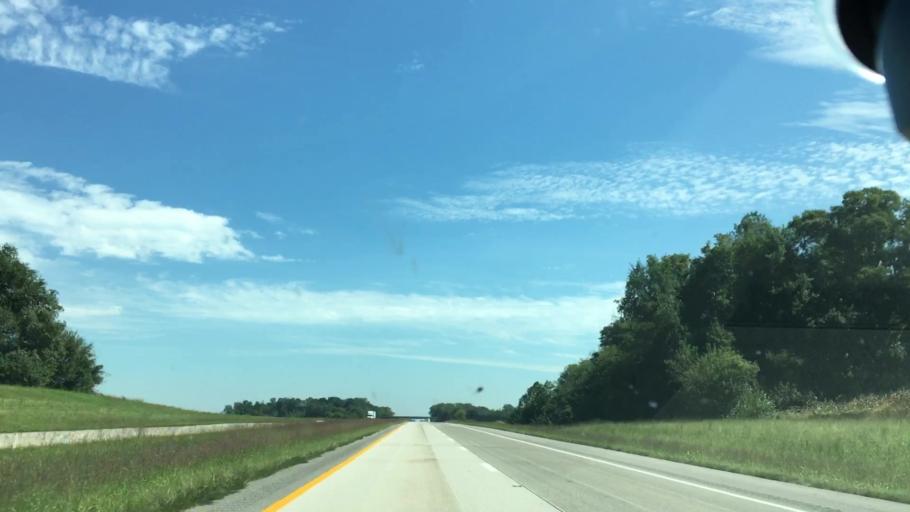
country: US
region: Kentucky
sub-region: Henderson County
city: Henderson
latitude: 37.7973
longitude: -87.5054
